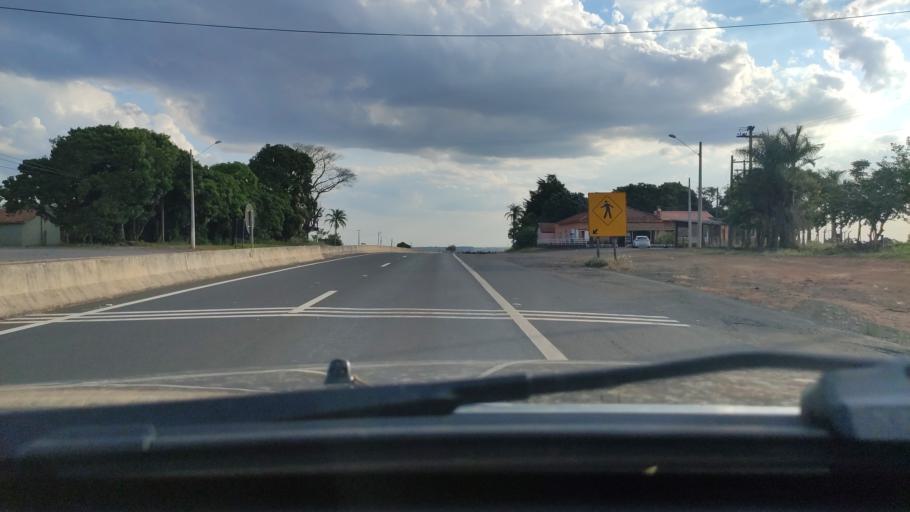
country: BR
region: Sao Paulo
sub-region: Artur Nogueira
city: Artur Nogueira
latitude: -22.4662
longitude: -47.1083
